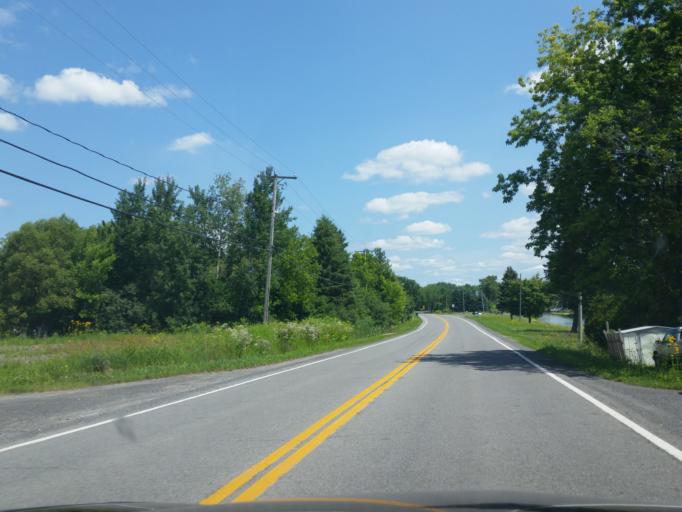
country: CA
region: Quebec
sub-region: Monteregie
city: Richelieu
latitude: 45.4043
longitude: -73.2578
